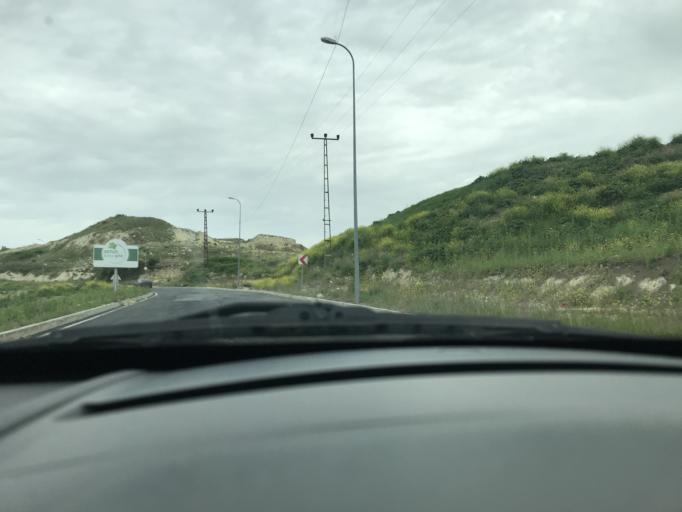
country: TR
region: Istanbul
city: Esenyurt
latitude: 41.0947
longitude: 28.6801
